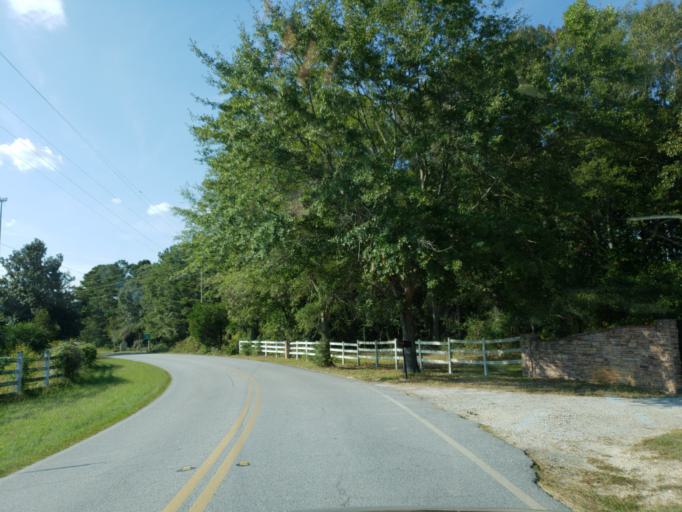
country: US
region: Georgia
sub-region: Paulding County
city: Hiram
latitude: 33.8787
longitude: -84.7238
